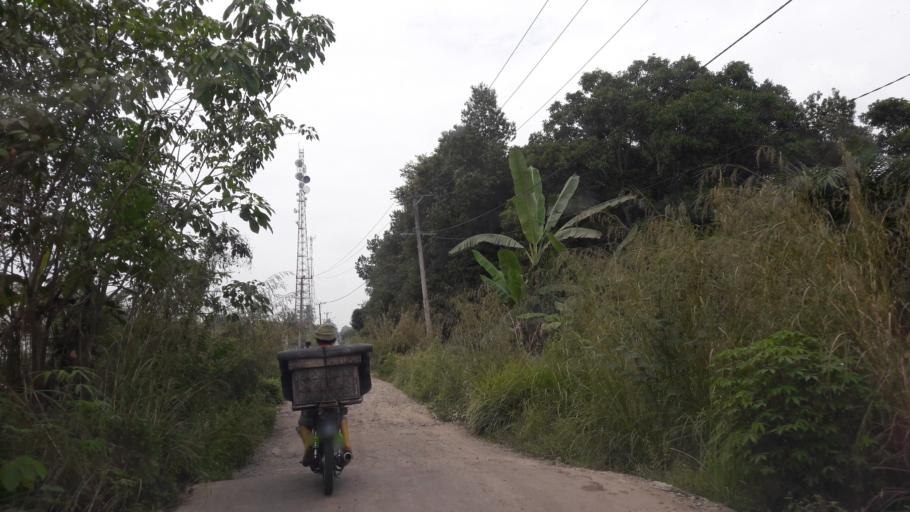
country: ID
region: South Sumatra
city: Gunungmenang
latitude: -3.2203
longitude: 104.0552
